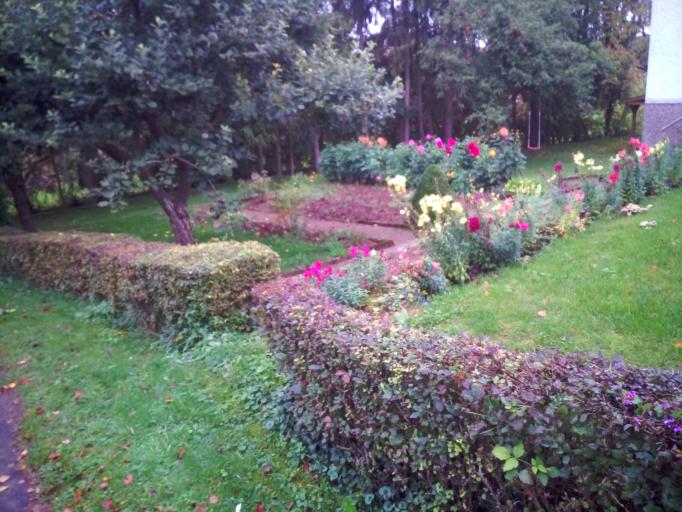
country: DE
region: Rheinland-Pfalz
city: Niederstedem
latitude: 49.9382
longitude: 6.4926
